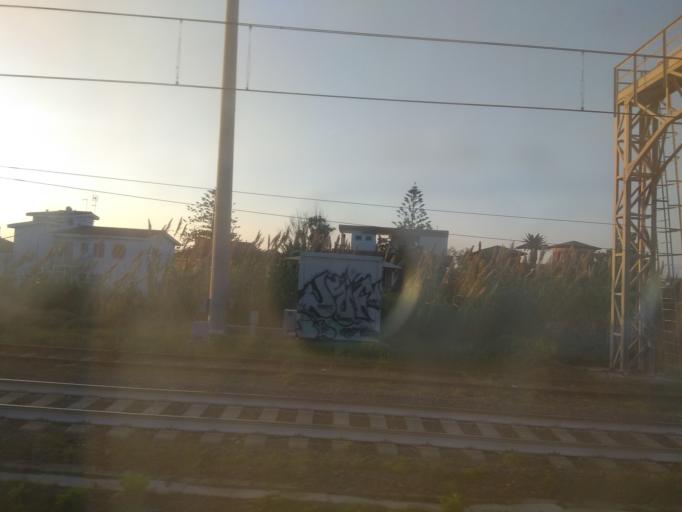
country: IT
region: Latium
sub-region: Citta metropolitana di Roma Capitale
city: Santa Marinella
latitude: 42.0356
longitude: 11.8609
